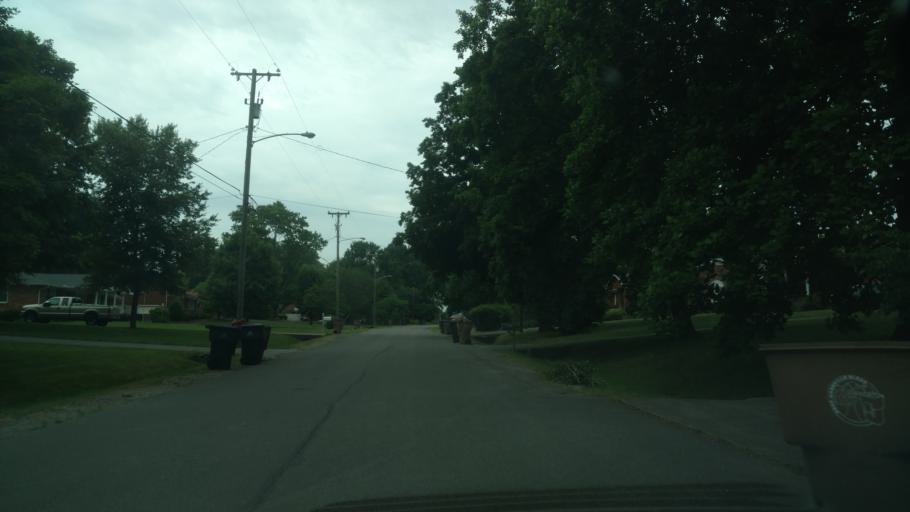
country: US
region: Tennessee
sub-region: Davidson County
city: Nashville
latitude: 36.1978
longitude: -86.7101
